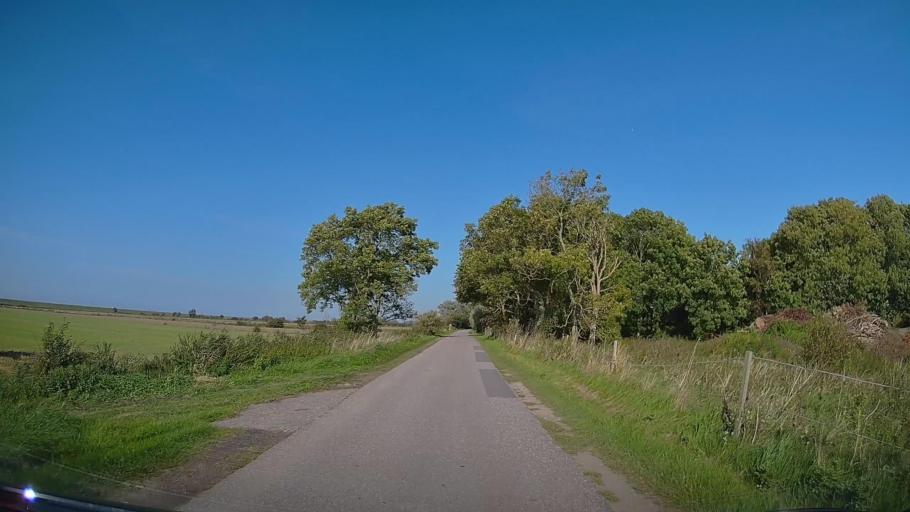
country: DE
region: Lower Saxony
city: Misselwarden
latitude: 53.7012
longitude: 8.4980
